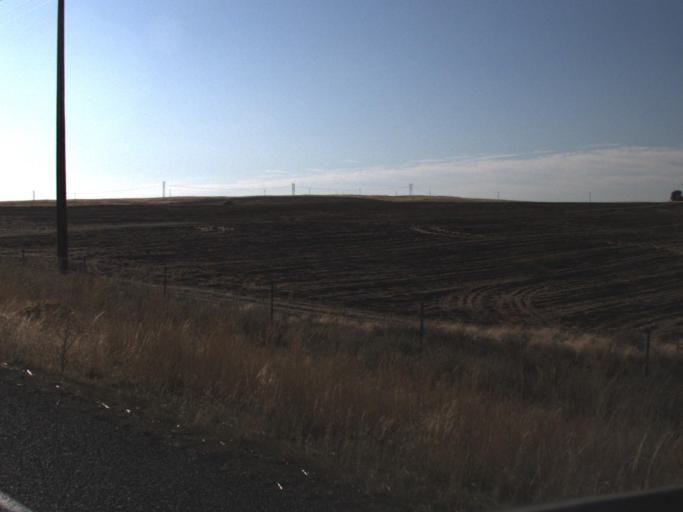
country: US
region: Washington
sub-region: Walla Walla County
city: Burbank
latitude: 46.2807
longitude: -118.7526
